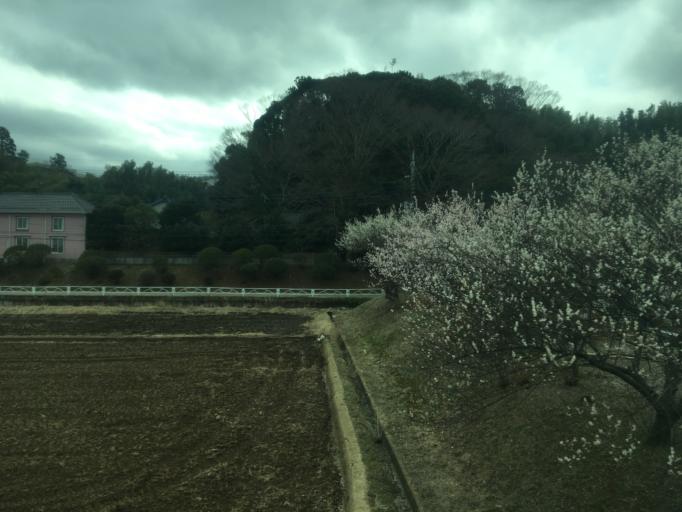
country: JP
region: Ibaraki
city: Ryugasaki
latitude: 35.8336
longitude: 140.1879
